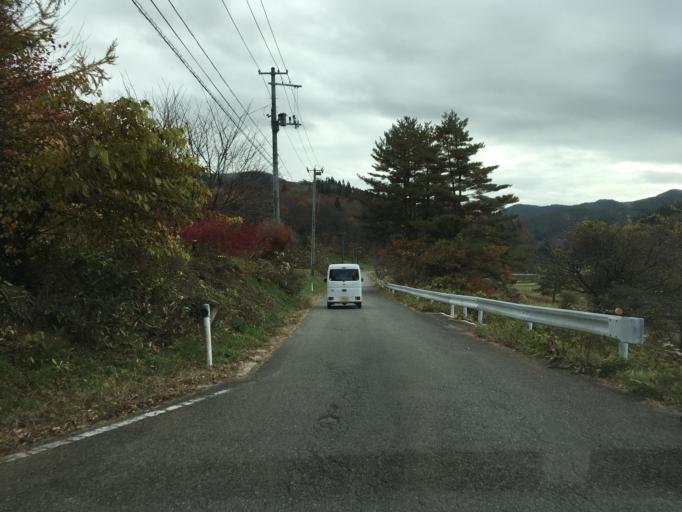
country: JP
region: Iwate
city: Mizusawa
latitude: 39.1174
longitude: 141.3242
